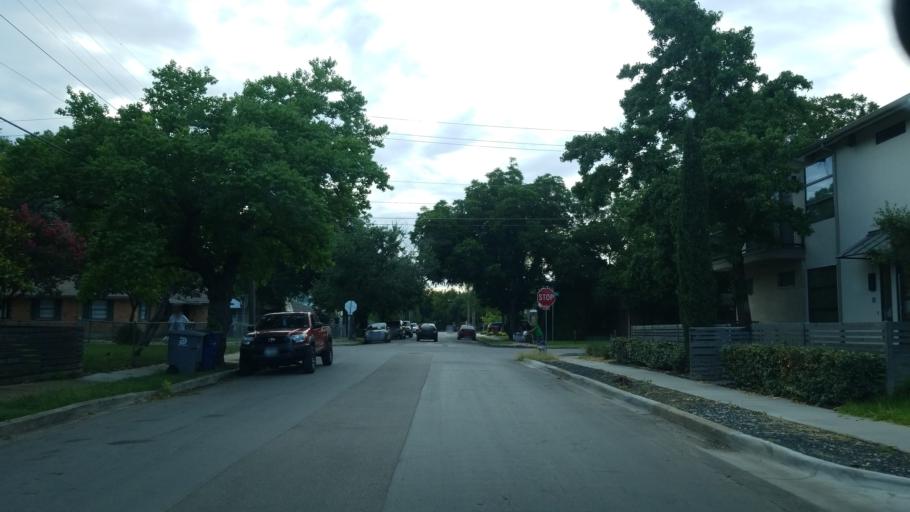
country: US
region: Texas
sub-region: Dallas County
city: Highland Park
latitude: 32.8091
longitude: -96.7813
